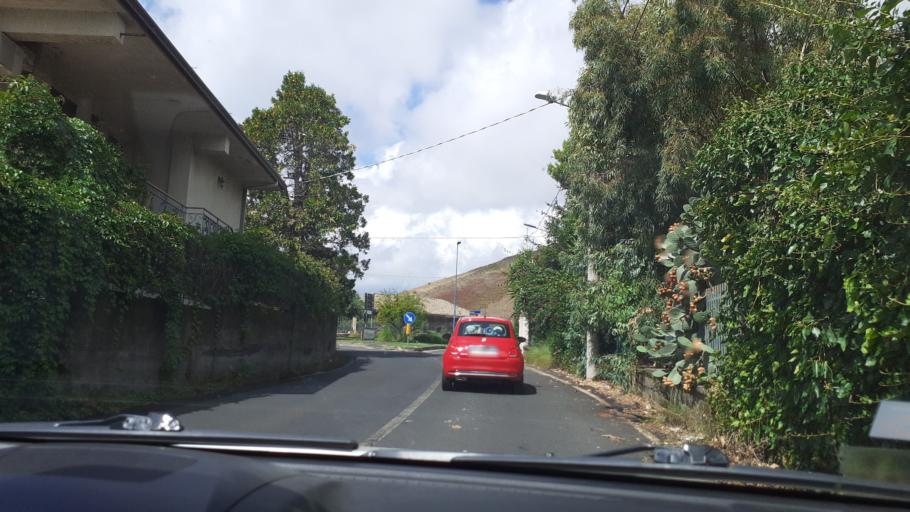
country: IT
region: Sicily
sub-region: Catania
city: Trecastagni
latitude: 37.6084
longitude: 15.0657
